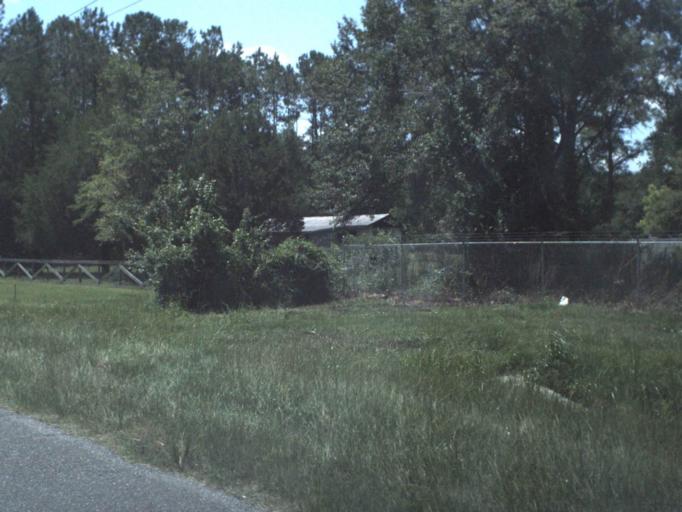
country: US
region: Florida
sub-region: Bradford County
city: Starke
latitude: 29.9637
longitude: -82.1816
